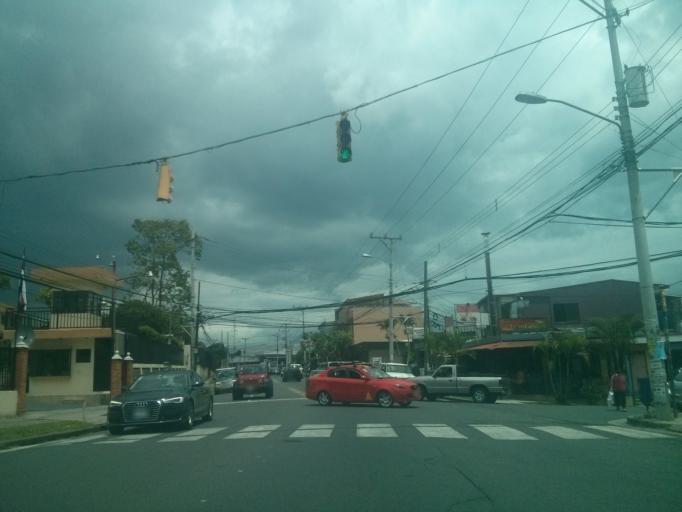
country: CR
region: San Jose
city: San Pedro
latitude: 9.9258
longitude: -84.0629
